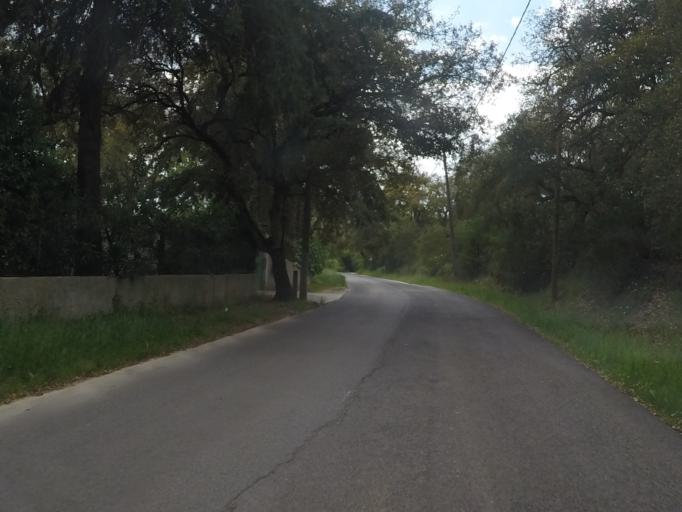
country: PT
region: Setubal
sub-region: Palmela
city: Quinta do Anjo
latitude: 38.5061
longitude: -8.9793
